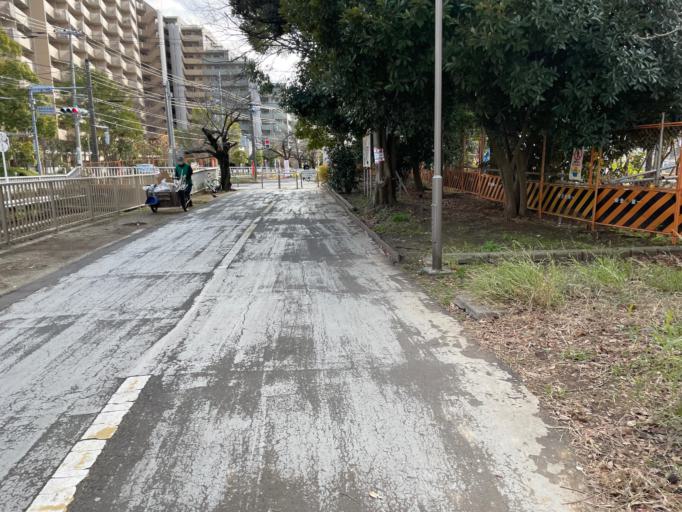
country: JP
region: Tokyo
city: Urayasu
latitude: 35.6807
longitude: 139.8389
